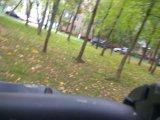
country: RU
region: Moscow
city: Kolomenskoye
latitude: 55.6819
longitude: 37.6897
